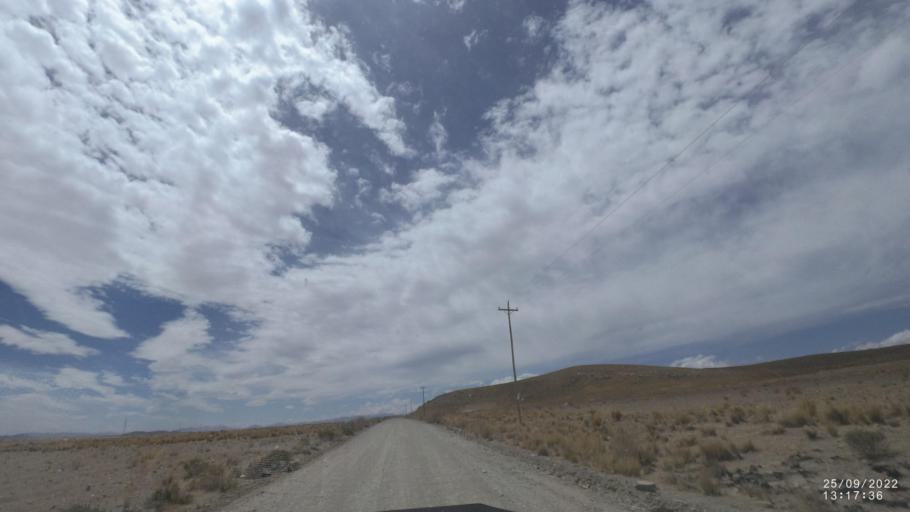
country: BO
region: Oruro
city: Oruro
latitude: -17.9070
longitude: -67.0440
